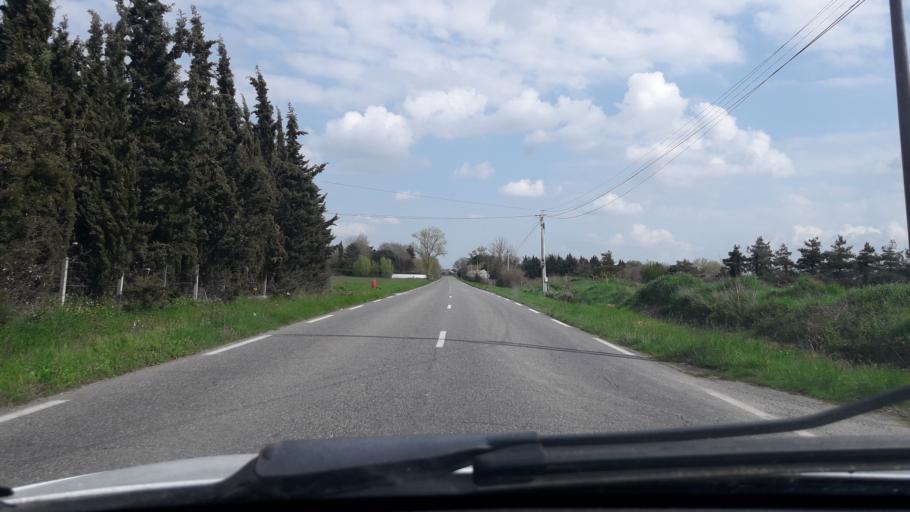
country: FR
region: Midi-Pyrenees
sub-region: Departement de la Haute-Garonne
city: Seysses
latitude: 43.5015
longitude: 1.2747
